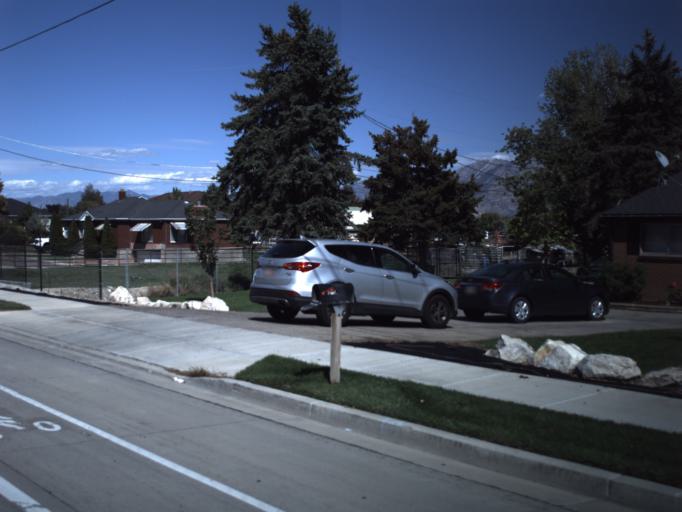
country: US
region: Utah
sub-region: Salt Lake County
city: Riverton
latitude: 40.5381
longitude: -111.9386
